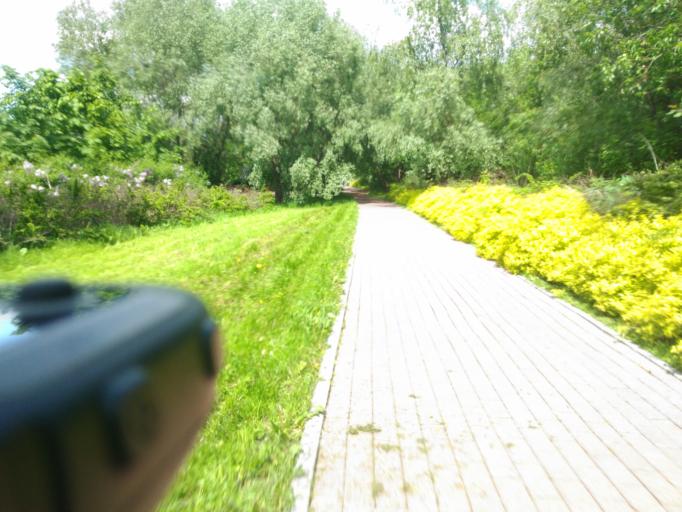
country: RU
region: Moscow
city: Shchukino
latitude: 55.7702
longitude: 37.4302
